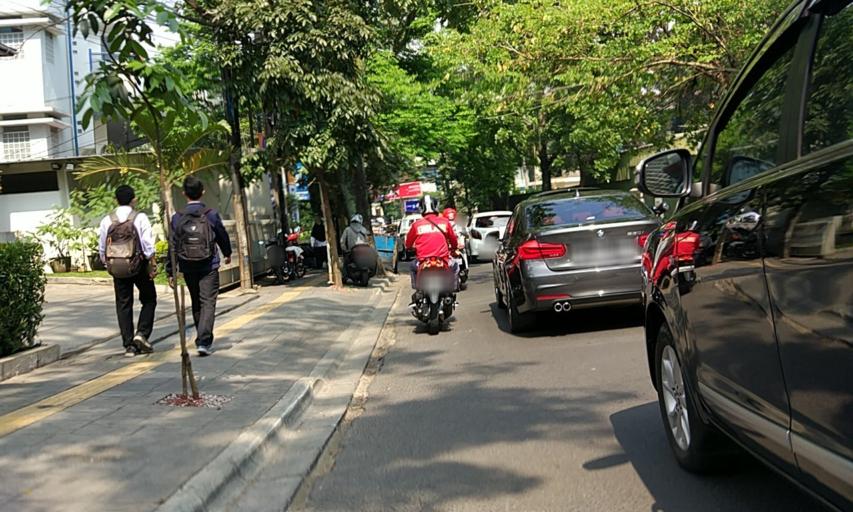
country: ID
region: West Java
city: Bandung
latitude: -6.9027
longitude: 107.6090
